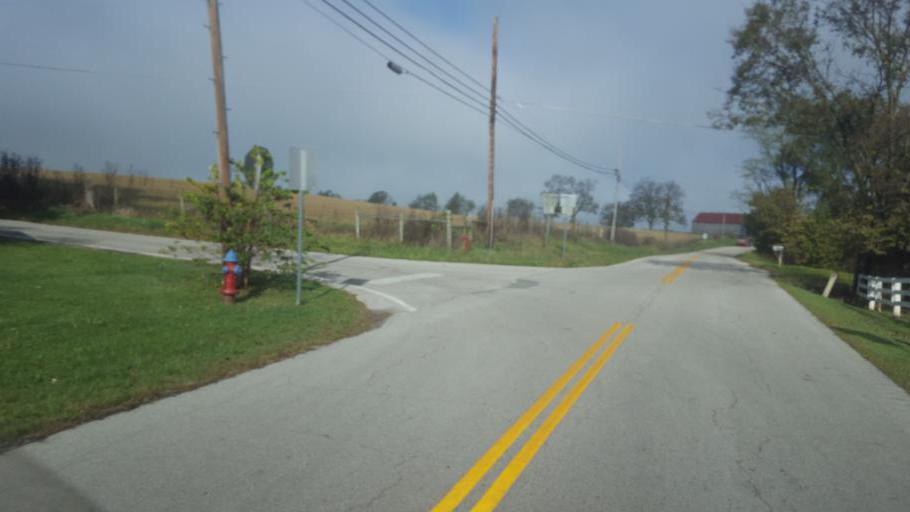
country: US
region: Kentucky
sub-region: Mason County
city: Maysville
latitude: 38.5623
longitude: -83.7761
